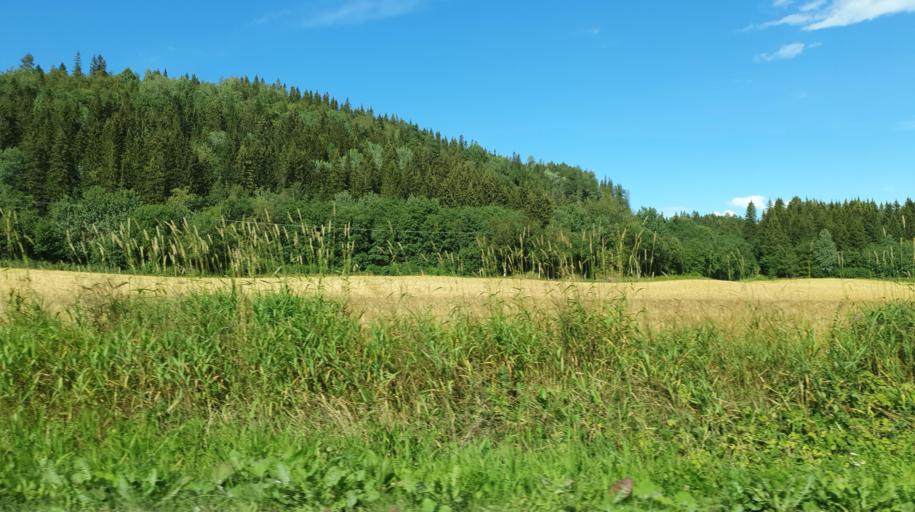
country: NO
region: Nord-Trondelag
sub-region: Levanger
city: Levanger
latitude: 63.6978
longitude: 11.2617
